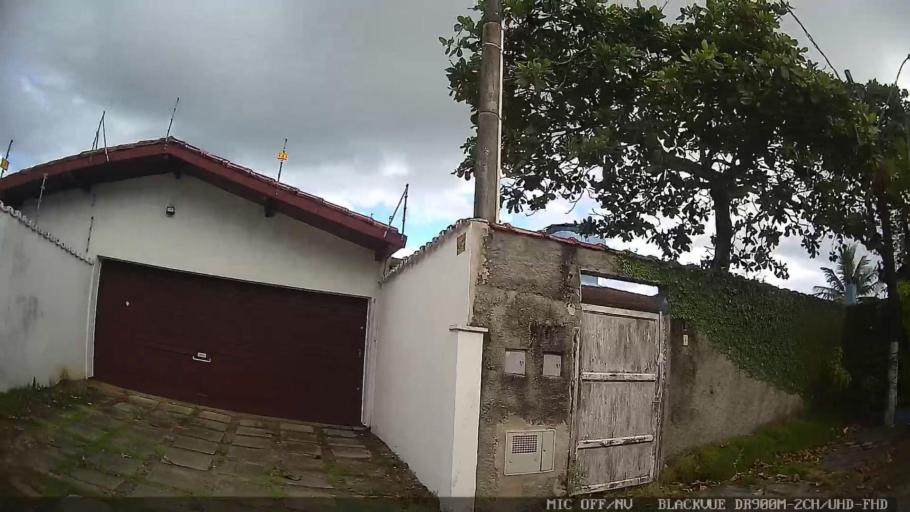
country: BR
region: Sao Paulo
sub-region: Itanhaem
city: Itanhaem
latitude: -24.1806
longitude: -46.7744
